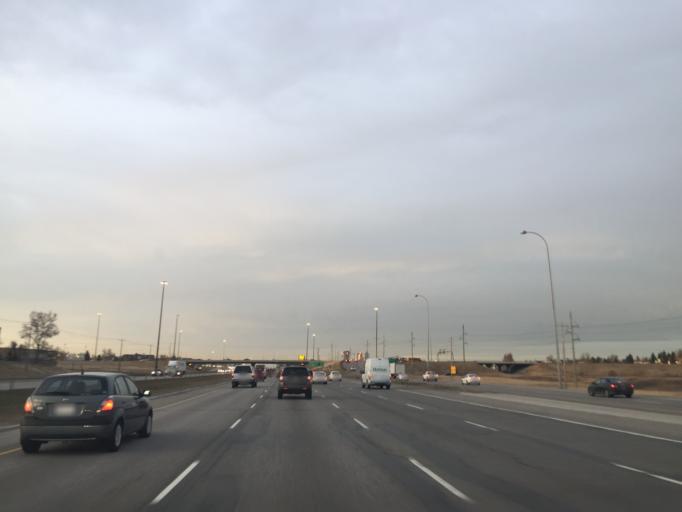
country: CA
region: Alberta
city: Calgary
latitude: 51.1146
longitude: -114.0472
